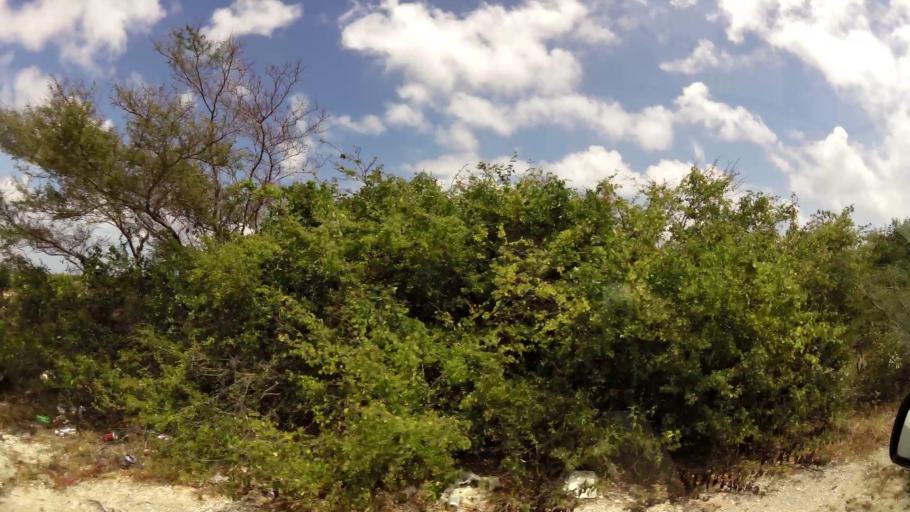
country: TC
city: Cockburn Town
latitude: 21.4593
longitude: -71.1385
